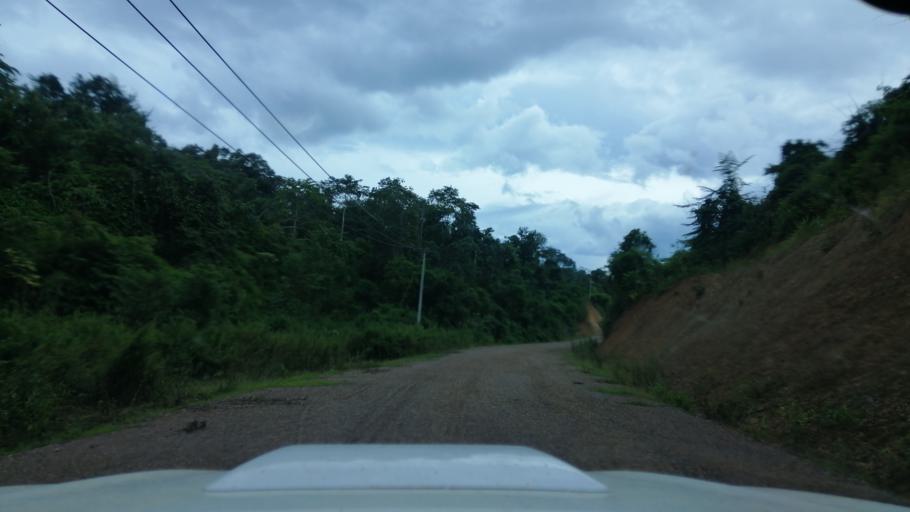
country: TH
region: Nan
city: Song Khwae
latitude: 19.5378
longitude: 100.7003
